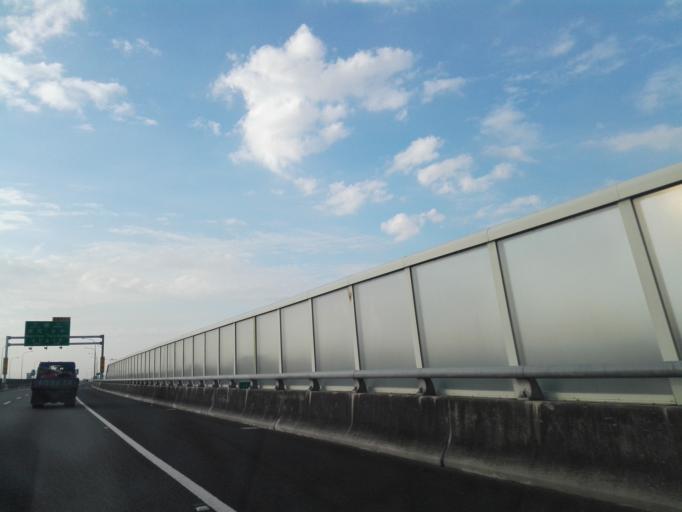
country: TW
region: Taiwan
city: Zhongxing New Village
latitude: 24.0156
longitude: 120.6897
